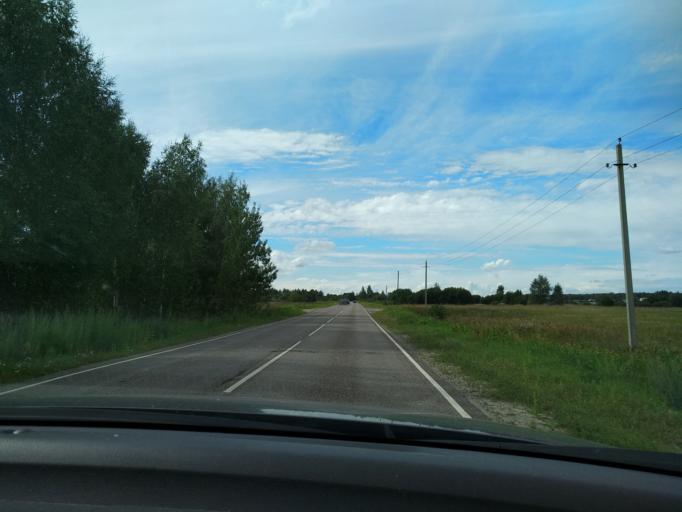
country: RU
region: Moskovskaya
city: Krasnyy Tkach
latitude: 55.3913
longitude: 39.1685
